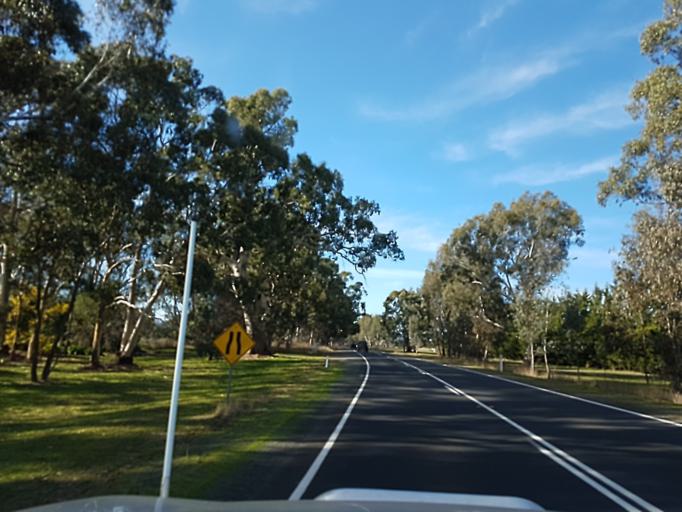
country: AU
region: Victoria
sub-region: Murrindindi
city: Alexandra
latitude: -37.1504
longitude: 145.6023
